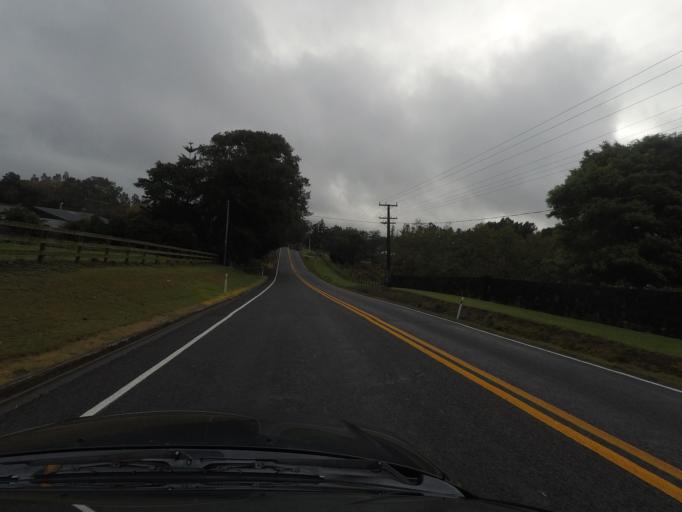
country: NZ
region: Auckland
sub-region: Auckland
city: Rosebank
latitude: -36.7794
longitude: 174.5864
